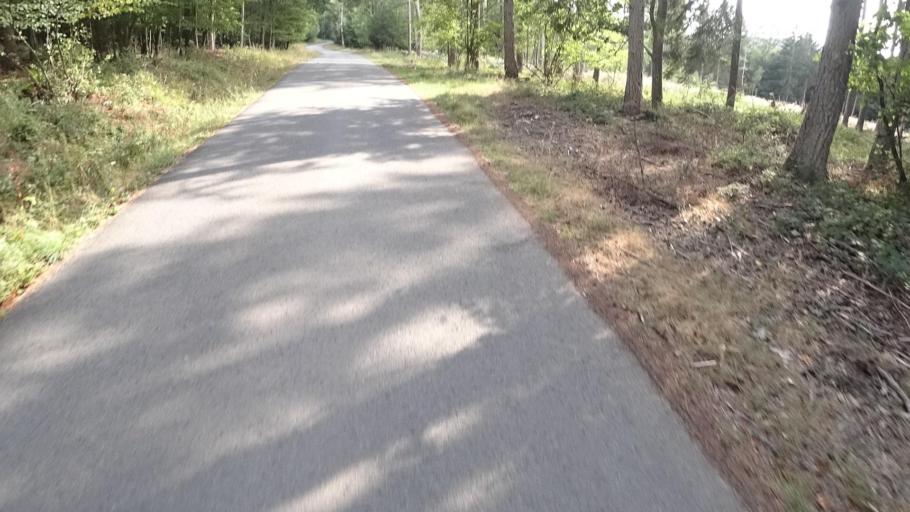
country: DE
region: Rheinland-Pfalz
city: Dichtelbach
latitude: 49.9977
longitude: 7.7048
